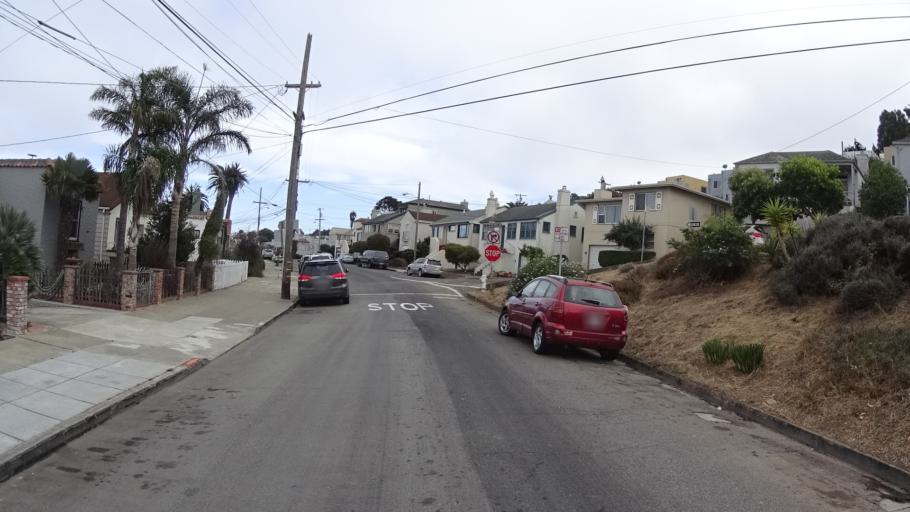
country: US
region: California
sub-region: San Mateo County
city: Daly City
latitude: 37.7103
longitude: -122.4380
